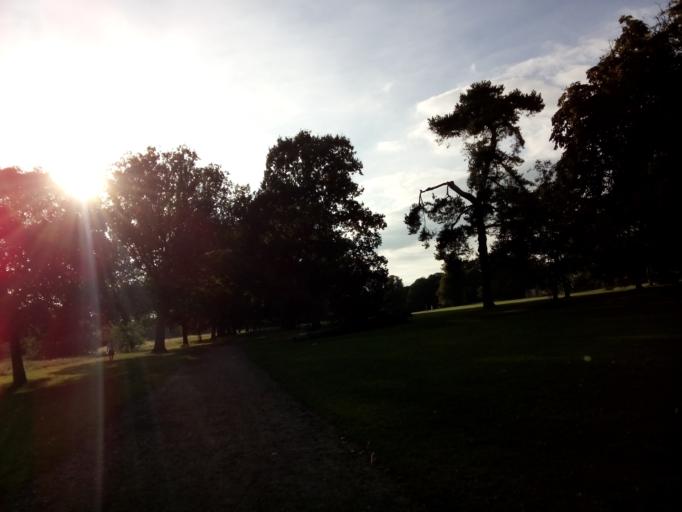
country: GB
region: England
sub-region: Suffolk
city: Ipswich
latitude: 52.0343
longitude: 1.1423
